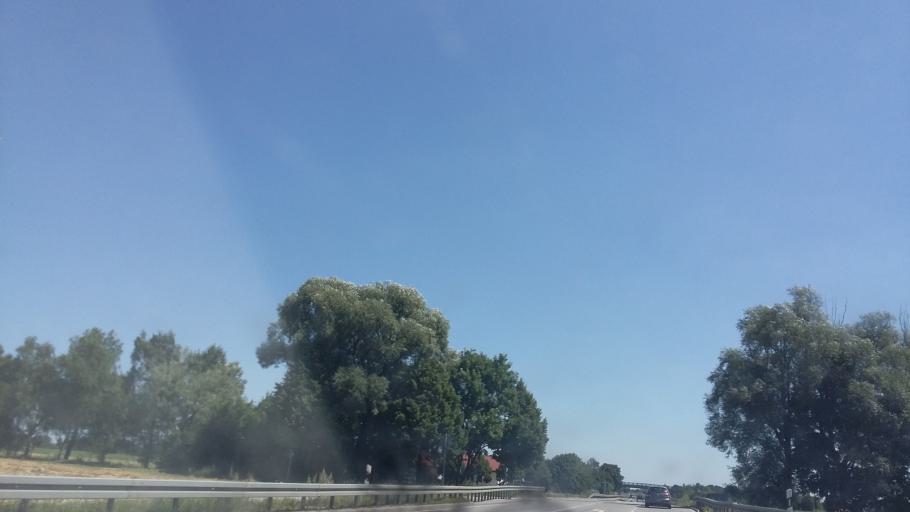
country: DE
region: Bavaria
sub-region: Upper Bavaria
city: Alling
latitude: 48.1519
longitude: 11.3094
